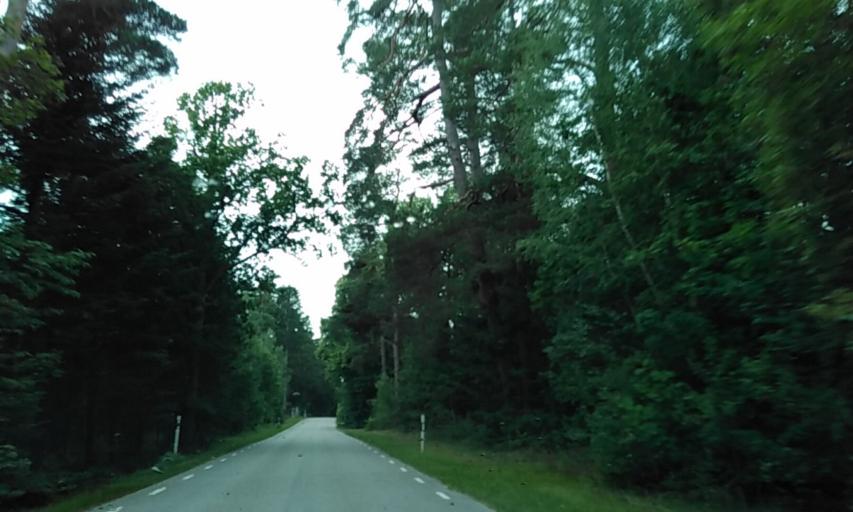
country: SE
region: Vaestra Goetaland
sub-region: Grastorps Kommun
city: Graestorp
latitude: 58.4628
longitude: 12.8041
